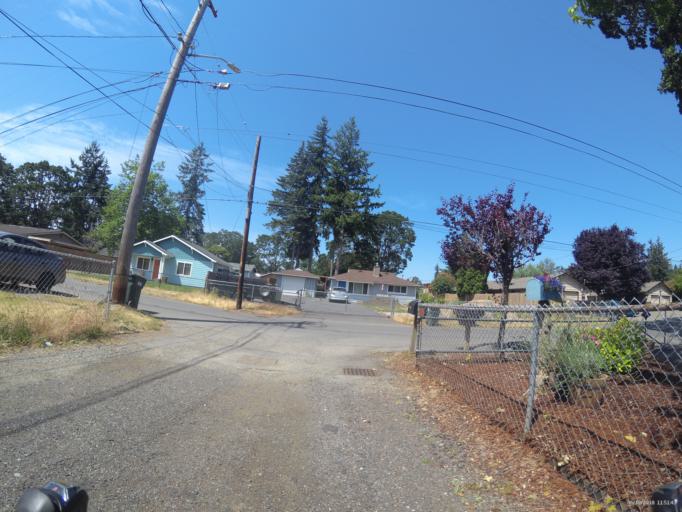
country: US
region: Washington
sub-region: Pierce County
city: Lakewood
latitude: 47.1790
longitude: -122.5262
